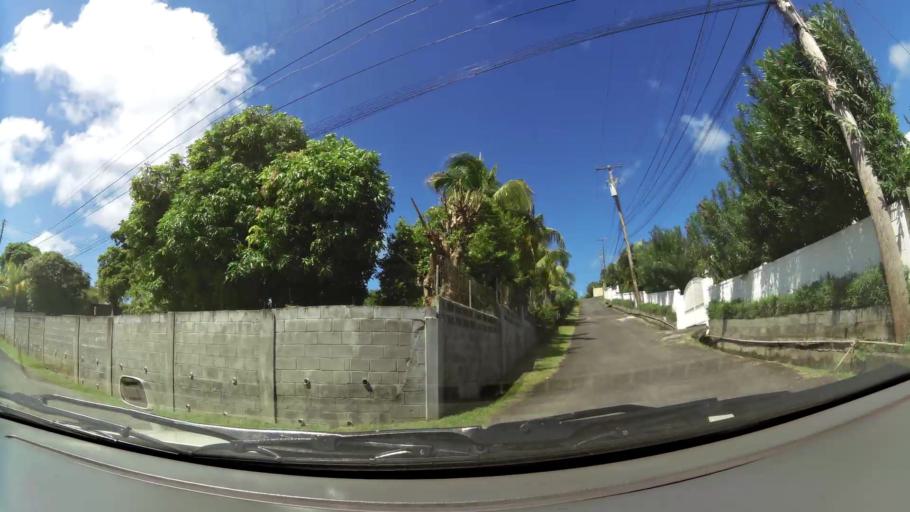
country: VC
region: Saint George
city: Kingstown
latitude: 13.1394
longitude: -61.2253
